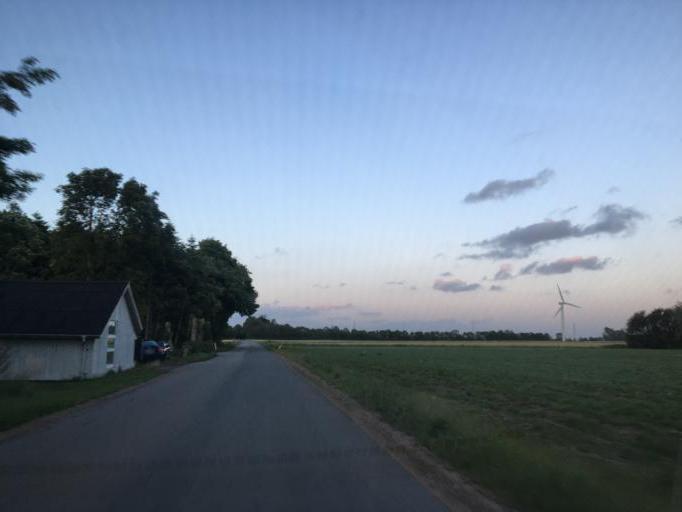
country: DK
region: Zealand
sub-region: Solrod Kommune
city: Havdrup
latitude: 55.5224
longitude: 12.0980
